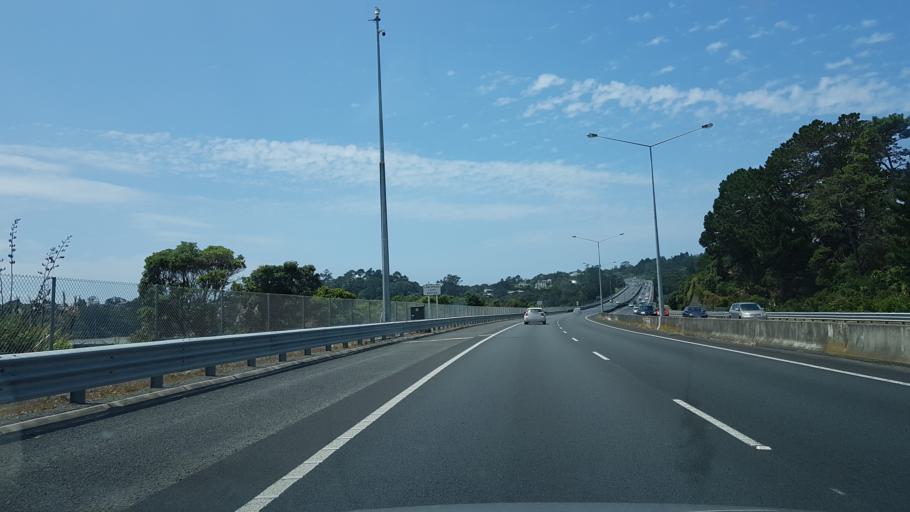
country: NZ
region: Auckland
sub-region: Auckland
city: Rosebank
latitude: -36.7867
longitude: 174.6617
